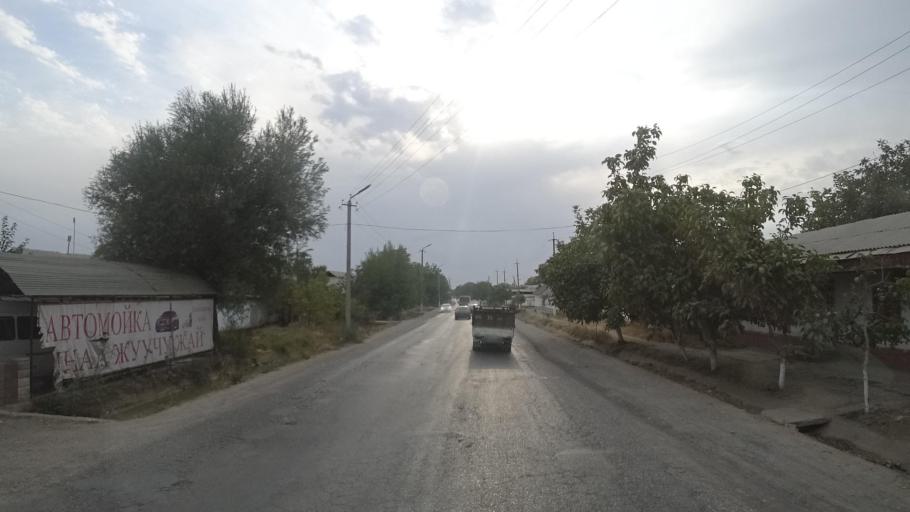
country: KG
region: Jalal-Abad
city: Massy
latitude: 41.0641
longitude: 72.6467
